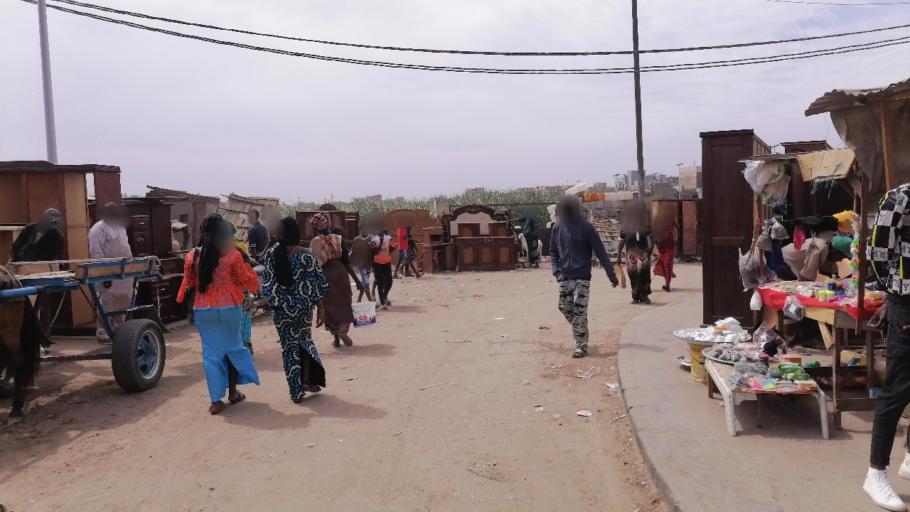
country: SN
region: Dakar
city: Pikine
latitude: 14.7754
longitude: -17.3731
